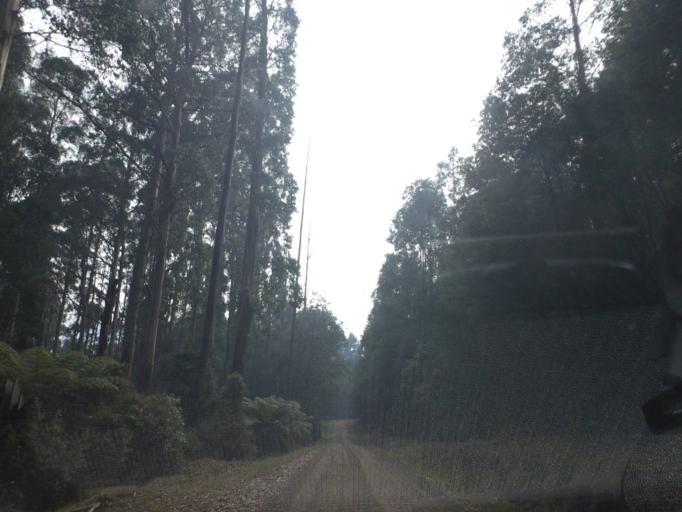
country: AU
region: Victoria
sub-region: Yarra Ranges
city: Healesville
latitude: -37.5602
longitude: 145.5360
